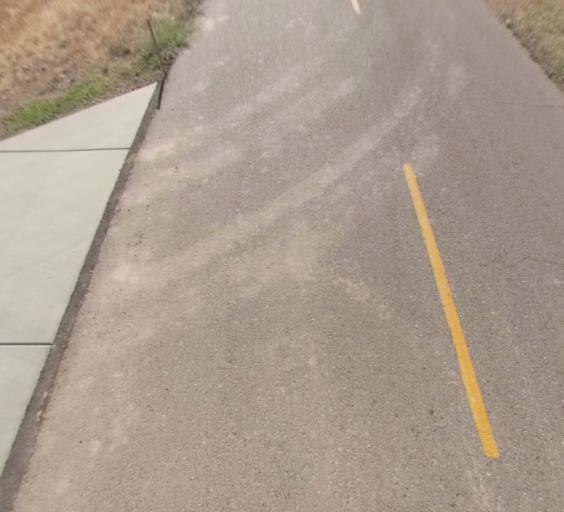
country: US
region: California
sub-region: Madera County
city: Bonadelle Ranchos-Madera Ranchos
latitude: 36.9724
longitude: -119.8837
